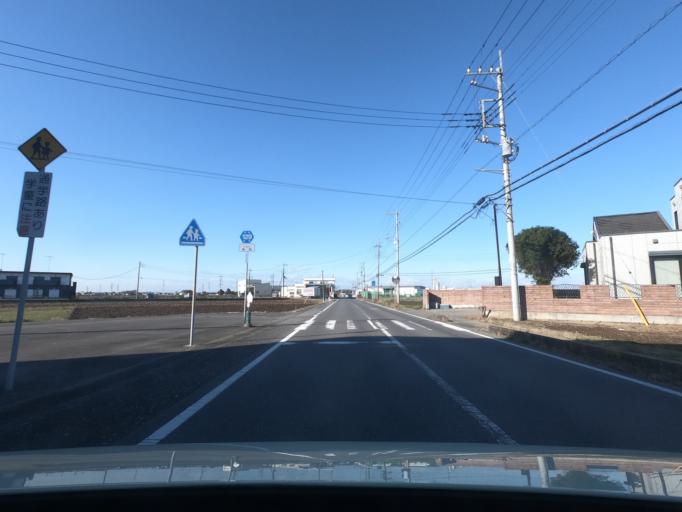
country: JP
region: Ibaraki
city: Ishige
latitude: 36.1634
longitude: 139.9922
